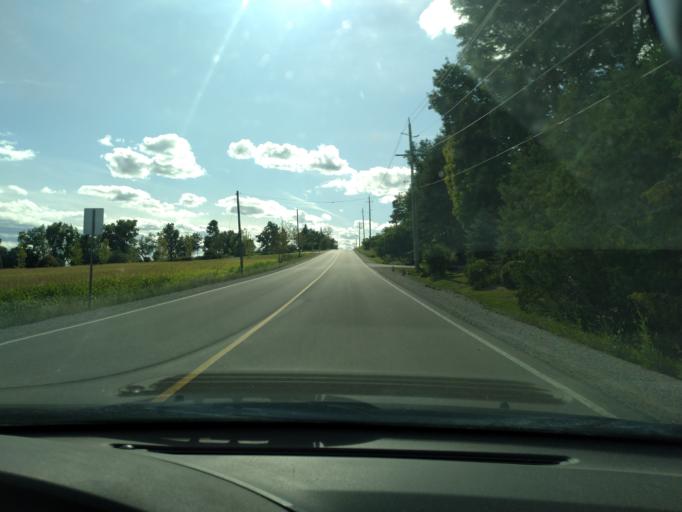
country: CA
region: Ontario
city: Bradford West Gwillimbury
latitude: 44.0817
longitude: -79.6528
